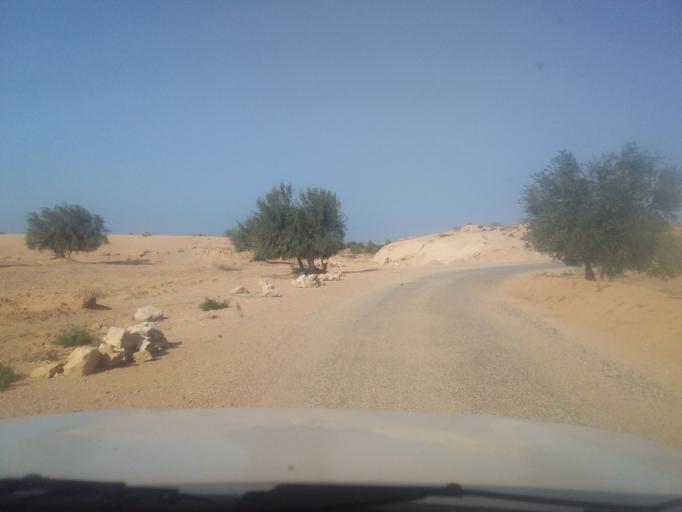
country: TN
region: Qabis
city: Matmata
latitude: 33.5848
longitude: 10.2583
